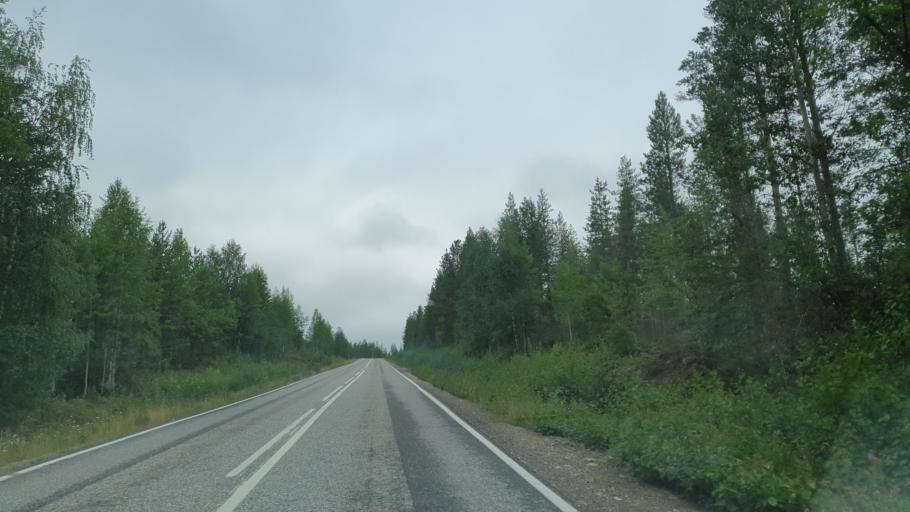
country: FI
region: Lapland
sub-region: Pohjois-Lappi
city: Sodankylae
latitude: 67.3761
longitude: 26.8491
